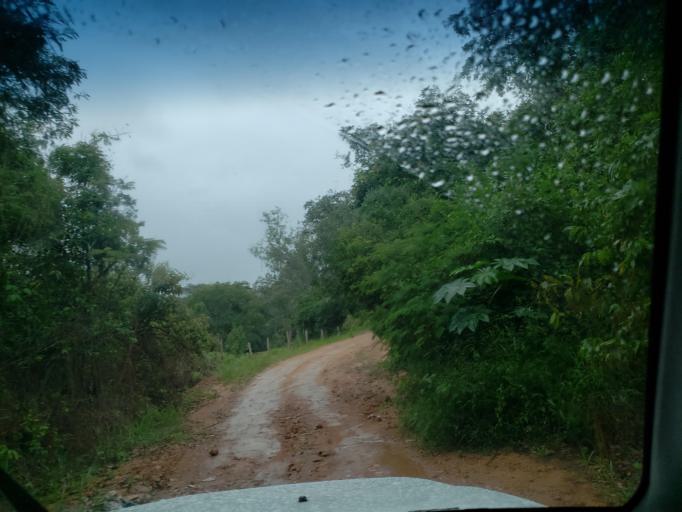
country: BR
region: Minas Gerais
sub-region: Monte Siao
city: Monte Siao
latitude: -22.3812
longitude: -46.5701
